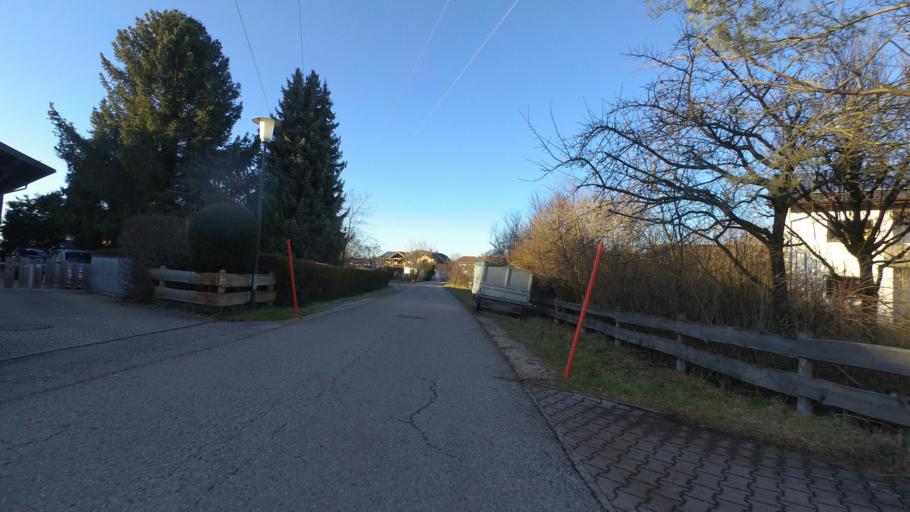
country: DE
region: Bavaria
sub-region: Upper Bavaria
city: Chieming
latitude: 47.9049
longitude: 12.5384
